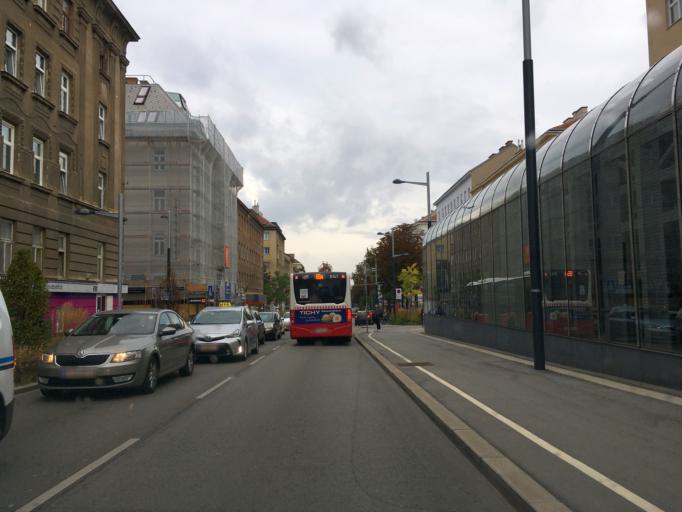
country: AT
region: Vienna
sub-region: Wien Stadt
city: Vienna
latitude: 48.1694
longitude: 16.3803
